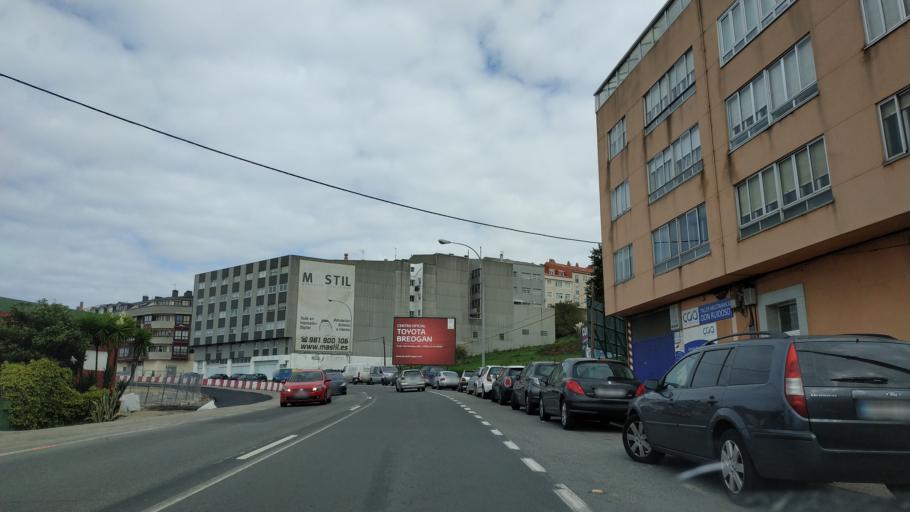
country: ES
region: Galicia
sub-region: Provincia da Coruna
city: Arteixo
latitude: 43.3110
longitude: -8.5014
